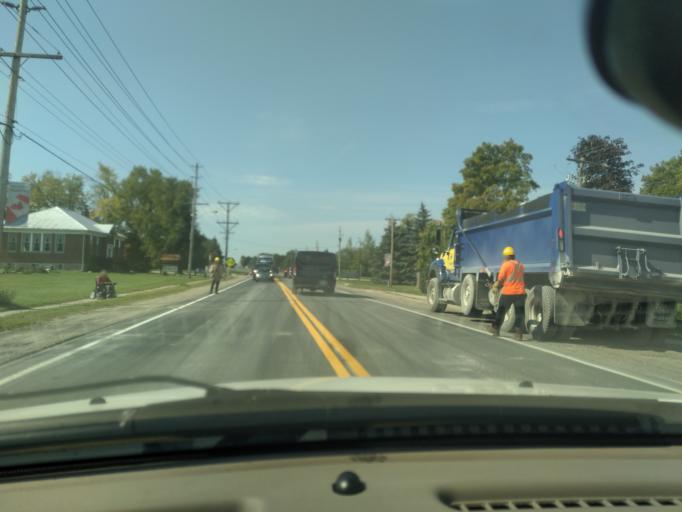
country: CA
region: Ontario
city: Innisfil
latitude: 44.2699
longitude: -79.7264
